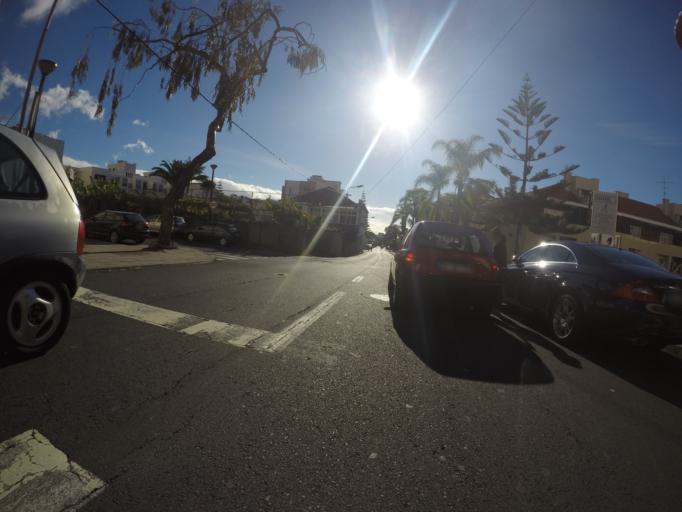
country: PT
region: Madeira
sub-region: Funchal
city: Nossa Senhora do Monte
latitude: 32.6592
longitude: -16.9301
